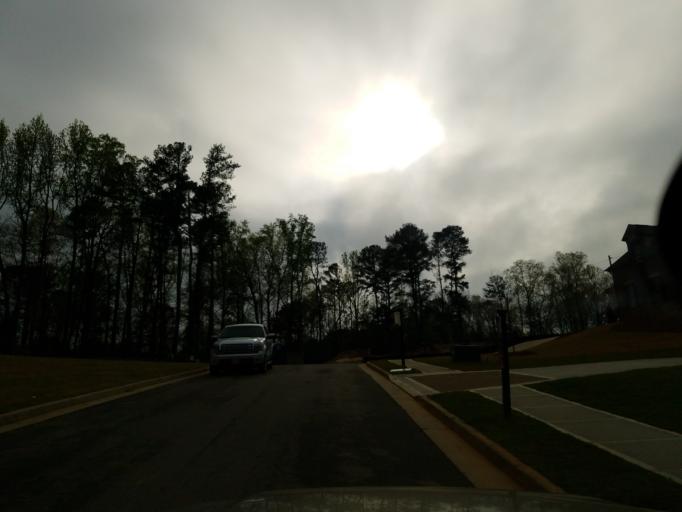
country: US
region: Georgia
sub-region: Fulton County
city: Roswell
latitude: 34.0172
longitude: -84.4146
